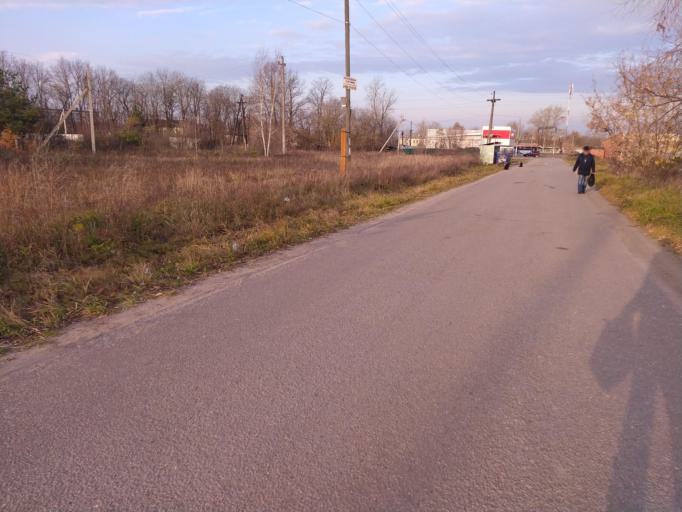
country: RU
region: Moskovskaya
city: Raduzhnyy
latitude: 55.1423
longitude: 38.7907
